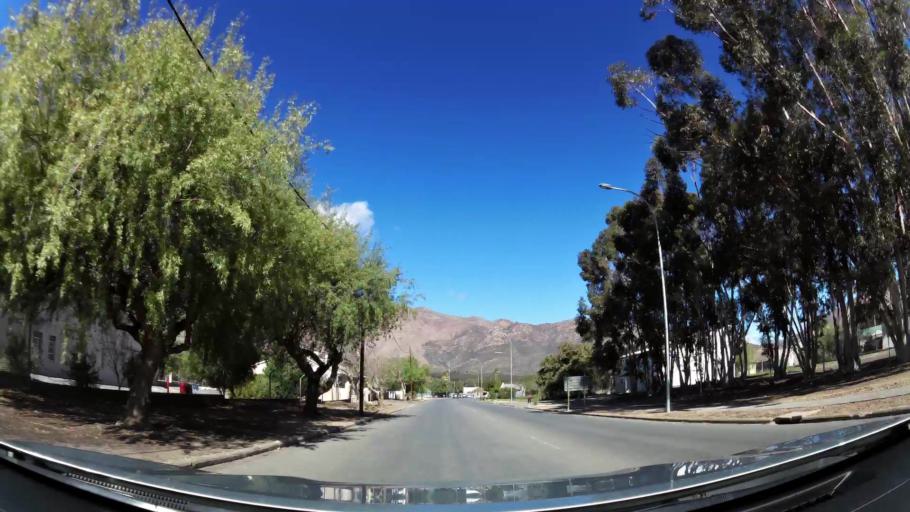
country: ZA
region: Western Cape
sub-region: Cape Winelands District Municipality
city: Ashton
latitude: -33.7826
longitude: 20.1302
